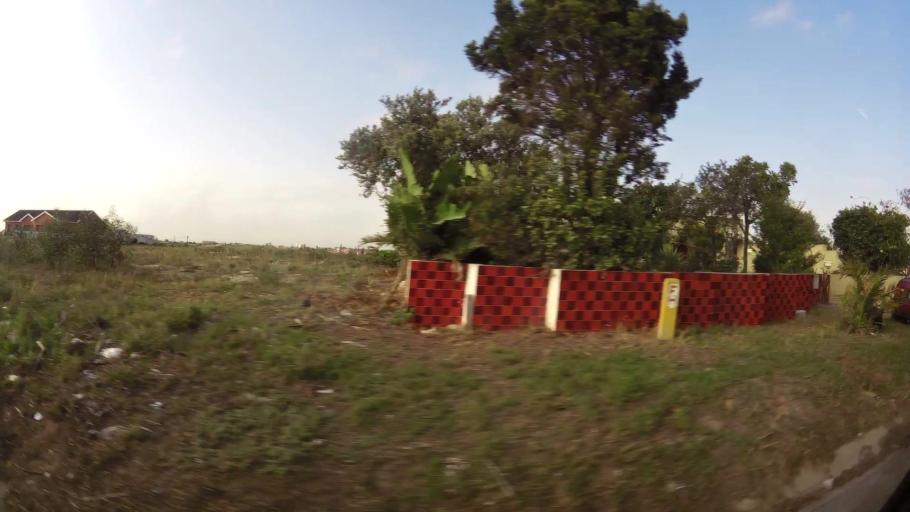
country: ZA
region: Eastern Cape
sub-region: Nelson Mandela Bay Metropolitan Municipality
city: Port Elizabeth
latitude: -33.9312
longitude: 25.5481
